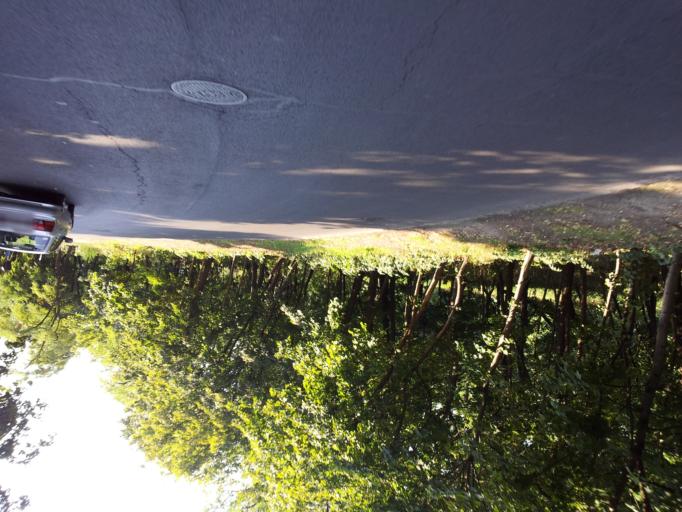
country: HU
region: Budapest
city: Budapest XX. keruelet
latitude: 47.4620
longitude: 19.1194
